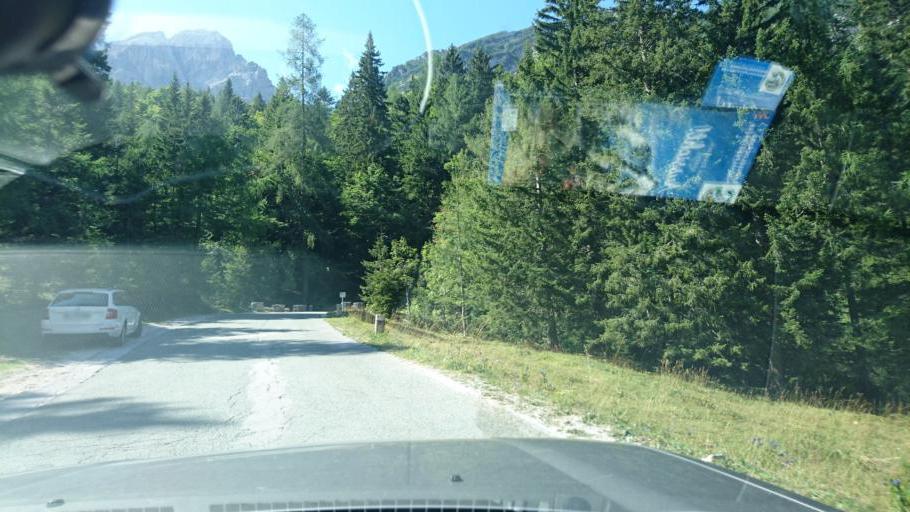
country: SI
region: Kranjska Gora
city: Kranjska Gora
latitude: 46.4392
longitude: 13.7539
